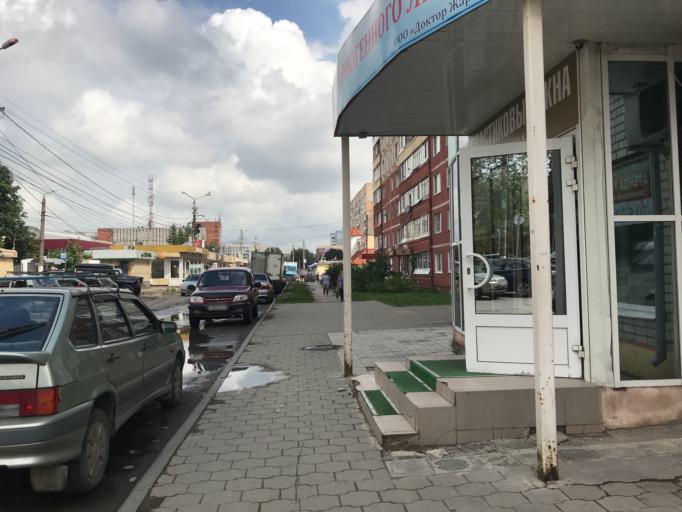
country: RU
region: Tula
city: Tula
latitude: 54.1985
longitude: 37.6438
